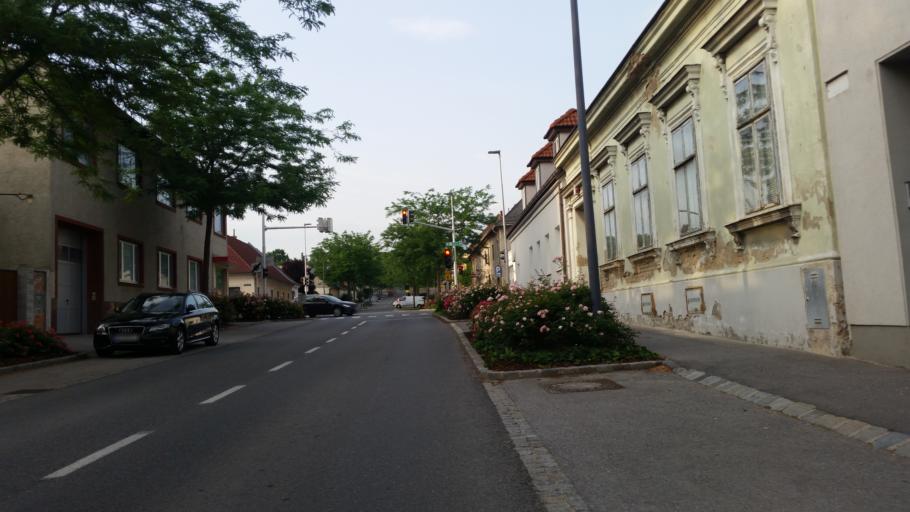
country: AT
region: Lower Austria
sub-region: Politischer Bezirk Mistelbach
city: Wolkersdorf im Weinviertel
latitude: 48.3859
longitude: 16.5164
